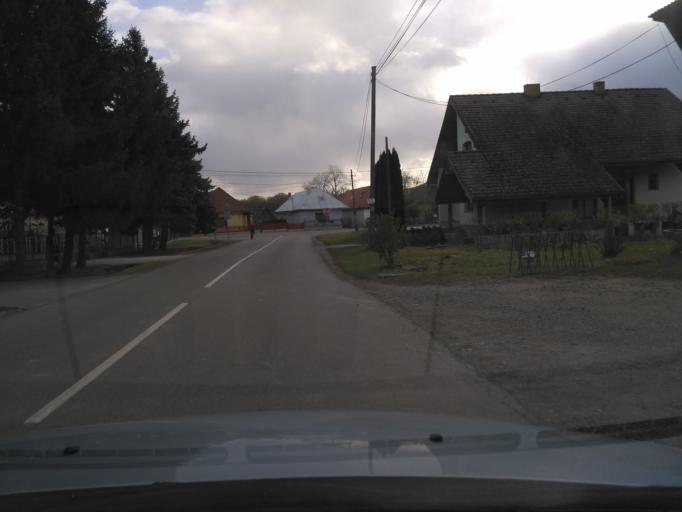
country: HU
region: Borsod-Abauj-Zemplen
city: Satoraljaujhely
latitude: 48.3962
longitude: 21.7094
